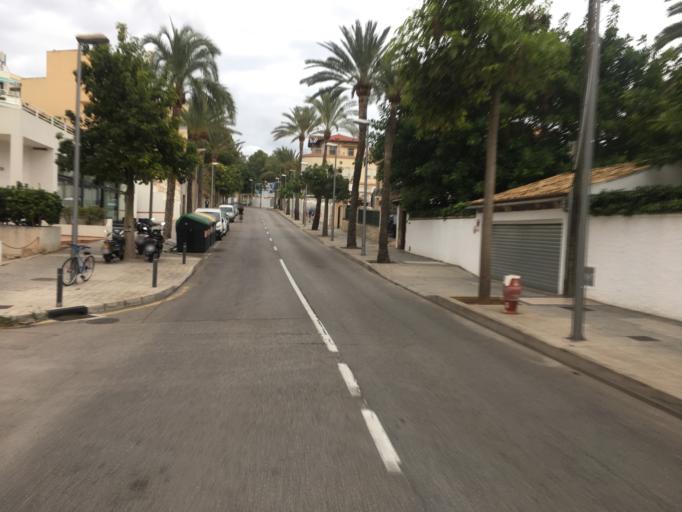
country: ES
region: Balearic Islands
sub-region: Illes Balears
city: Palma
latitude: 39.5514
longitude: 2.6094
